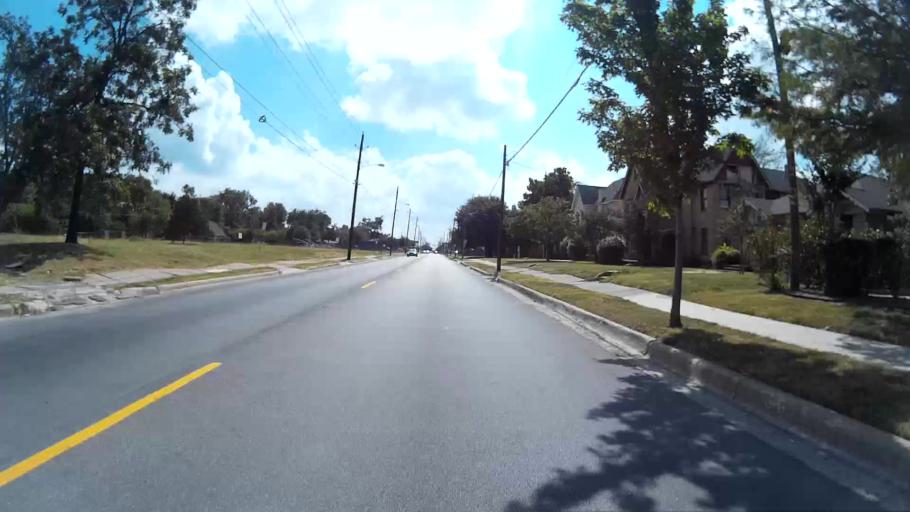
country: US
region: Texas
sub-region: Dallas County
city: Highland Park
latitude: 32.8139
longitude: -96.7775
